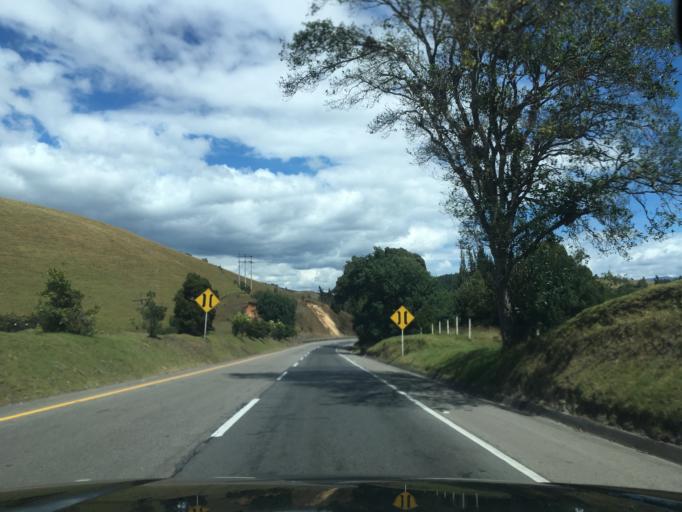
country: CO
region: Cundinamarca
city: Choconta
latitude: 5.0878
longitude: -73.7234
